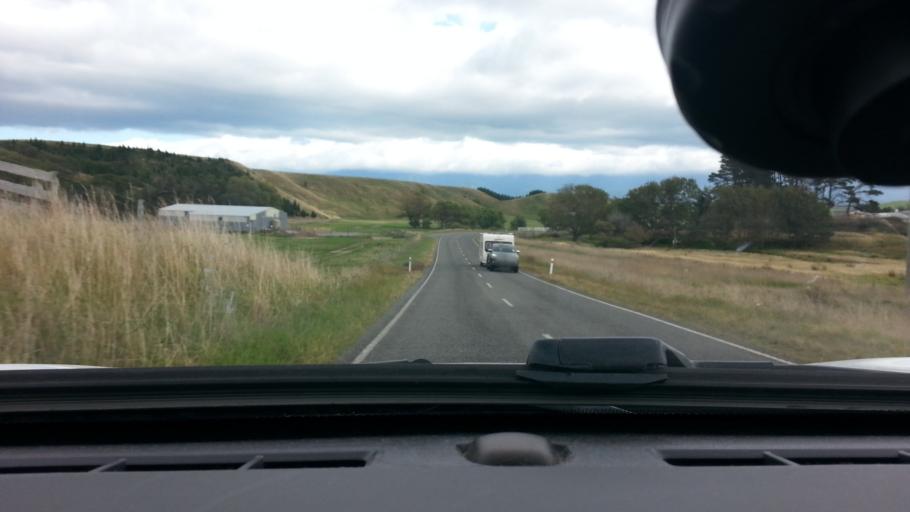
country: NZ
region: Wellington
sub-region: Upper Hutt City
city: Upper Hutt
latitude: -41.4152
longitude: 175.1994
